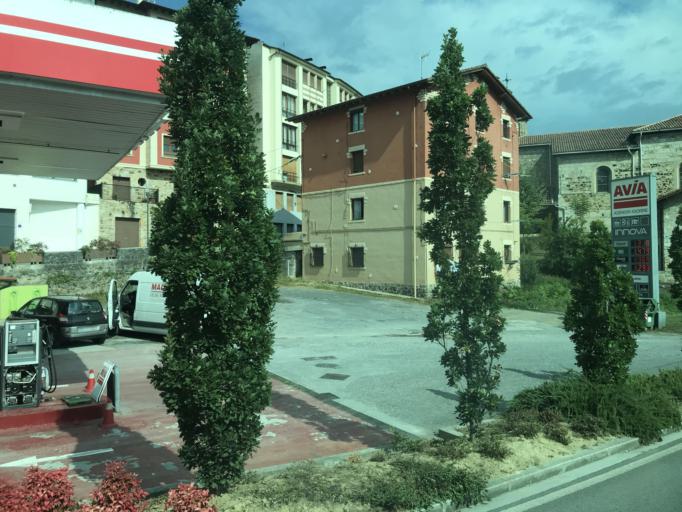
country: ES
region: Basque Country
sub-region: Bizkaia
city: Areatza
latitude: 43.1639
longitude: -2.7775
